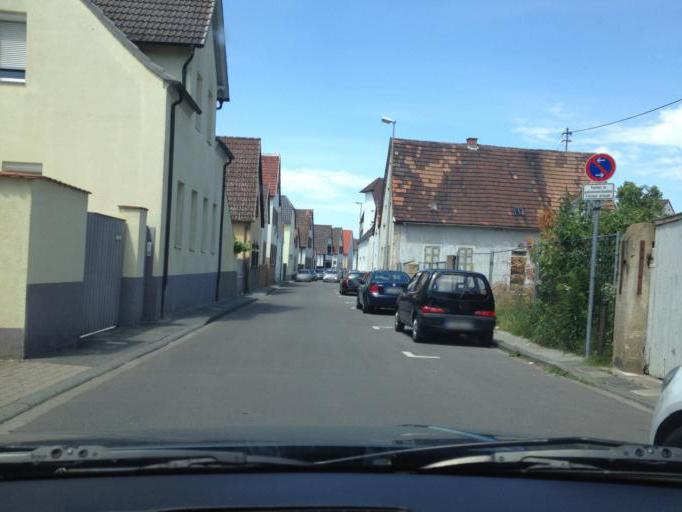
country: DE
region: Rheinland-Pfalz
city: Neuhofen
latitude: 49.4237
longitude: 8.4271
